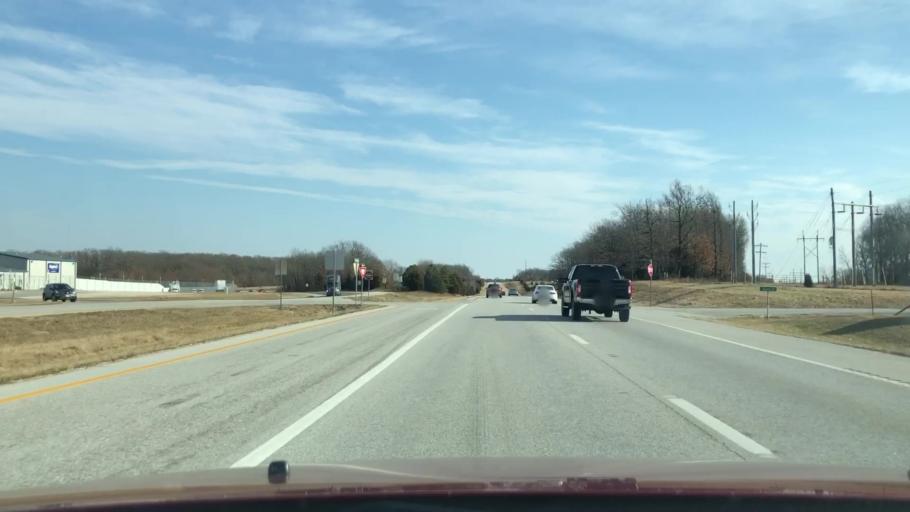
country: US
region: Missouri
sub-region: Webster County
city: Rogersville
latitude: 37.1186
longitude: -93.0145
